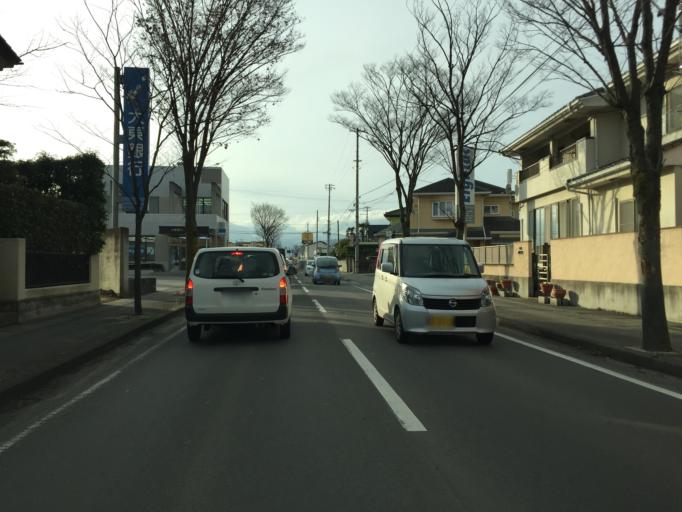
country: JP
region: Fukushima
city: Fukushima-shi
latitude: 37.7850
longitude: 140.4672
